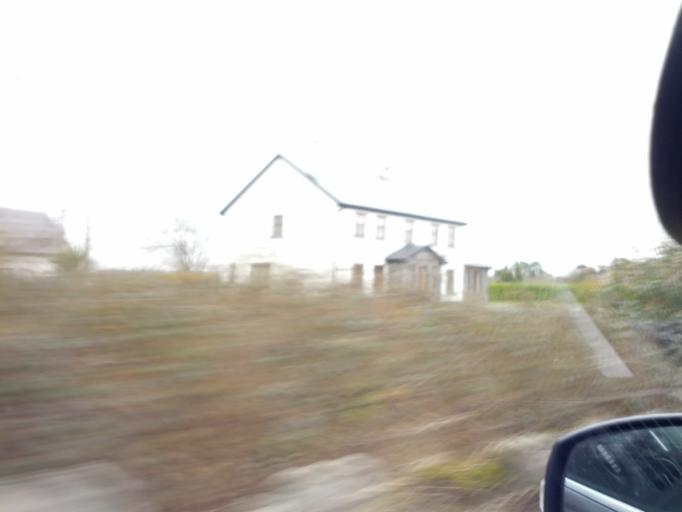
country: IE
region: Connaught
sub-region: County Galway
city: Athenry
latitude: 53.2681
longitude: -8.7429
